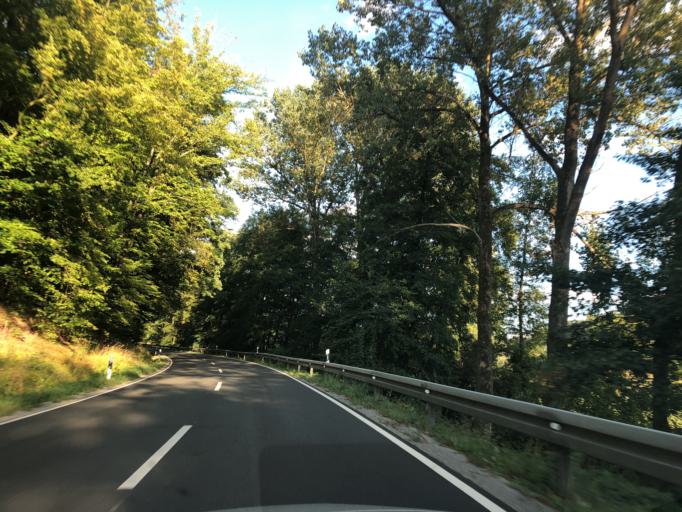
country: DE
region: Bavaria
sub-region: Upper Franconia
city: Burgwindheim
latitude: 49.8330
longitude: 10.5511
